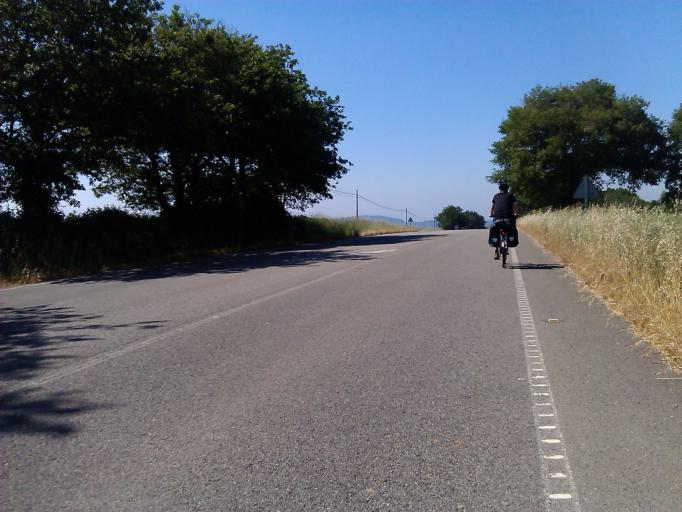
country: ES
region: Galicia
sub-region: Provincia de Lugo
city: Samos
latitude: 42.7417
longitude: -7.3711
